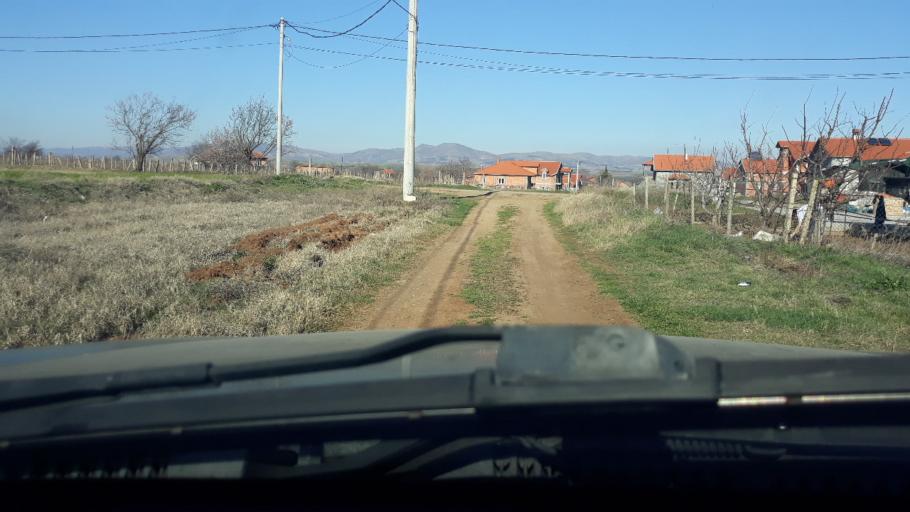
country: MK
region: Sveti Nikole
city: Sveti Nikole
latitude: 41.8708
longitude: 21.9312
